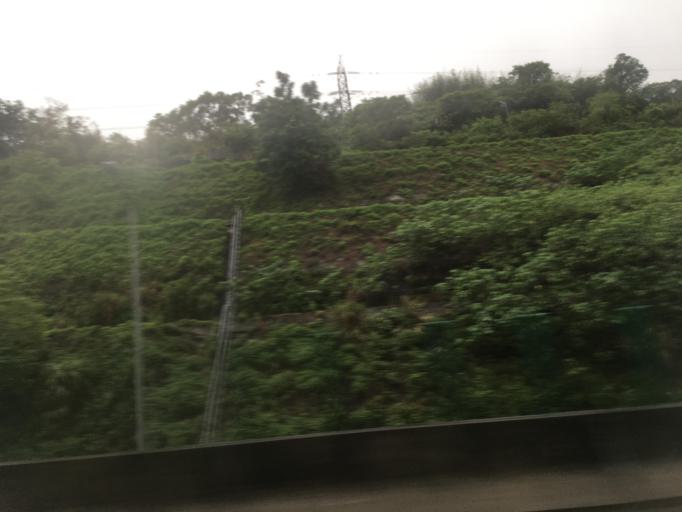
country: TW
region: Taipei
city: Taipei
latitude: 24.9957
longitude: 121.6523
